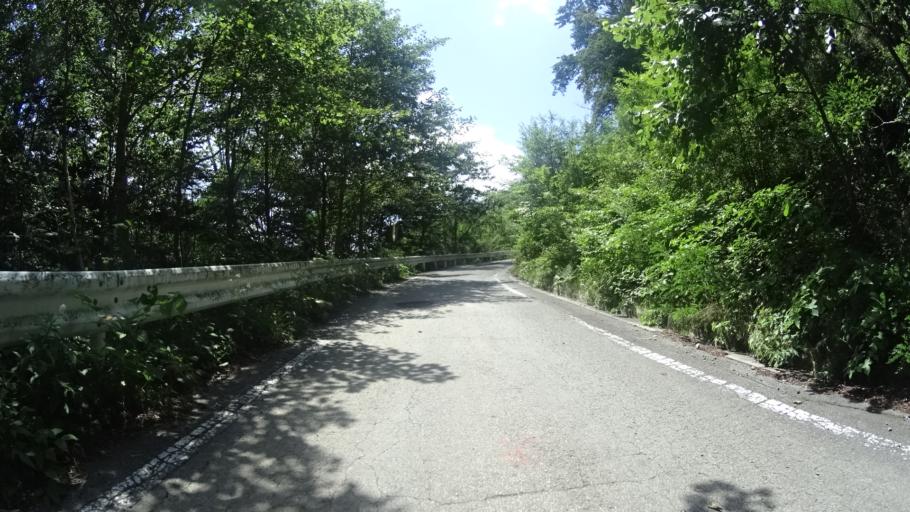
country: JP
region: Yamanashi
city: Enzan
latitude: 35.8218
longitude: 138.6538
